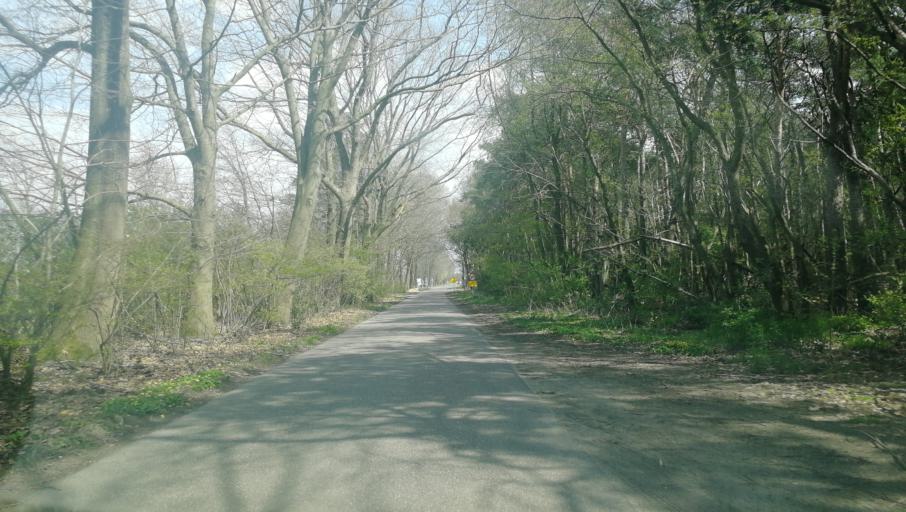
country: NL
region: Limburg
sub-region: Gemeente Venlo
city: Tegelen
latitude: 51.4080
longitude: 6.1104
